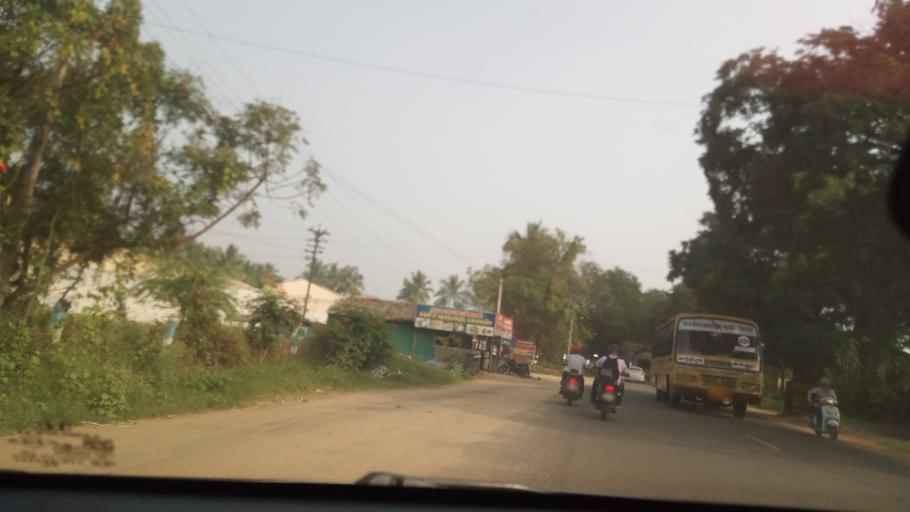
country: IN
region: Tamil Nadu
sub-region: Coimbatore
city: Annur
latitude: 11.1648
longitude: 77.0522
